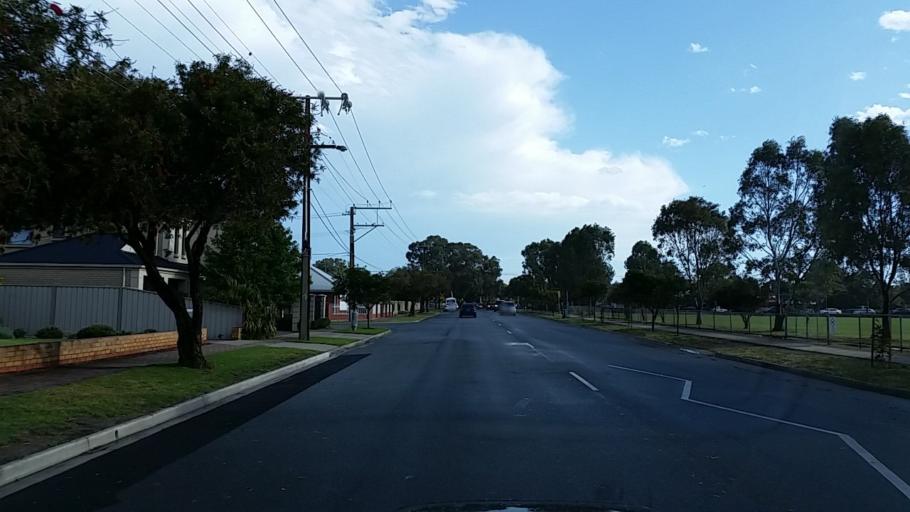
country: AU
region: South Australia
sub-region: Charles Sturt
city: Henley Beach
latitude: -34.9238
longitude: 138.5014
